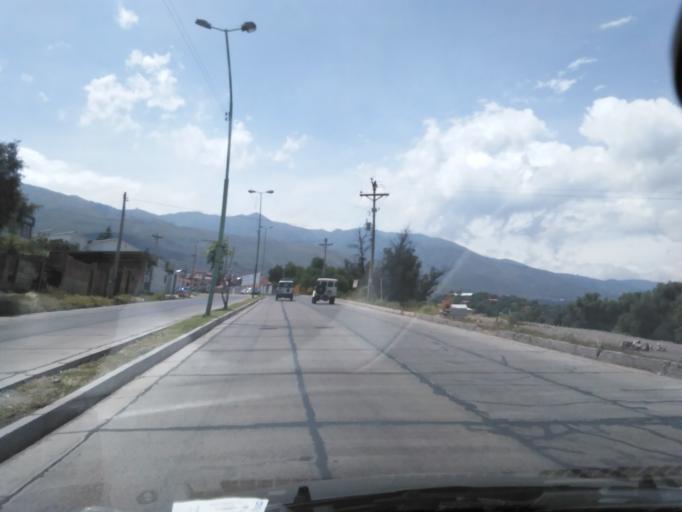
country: BO
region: Cochabamba
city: Cochabamba
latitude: -17.3753
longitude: -66.1378
